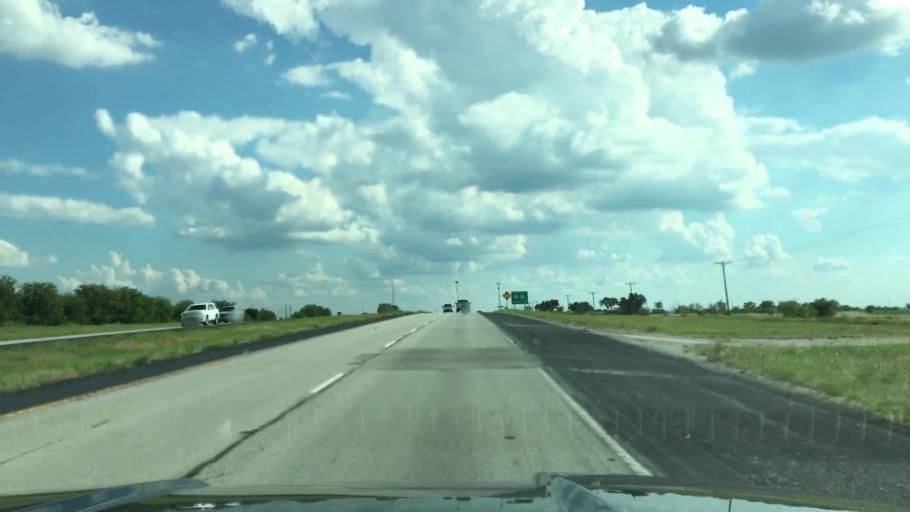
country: US
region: Texas
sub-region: Wise County
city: Rhome
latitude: 33.0749
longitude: -97.4732
